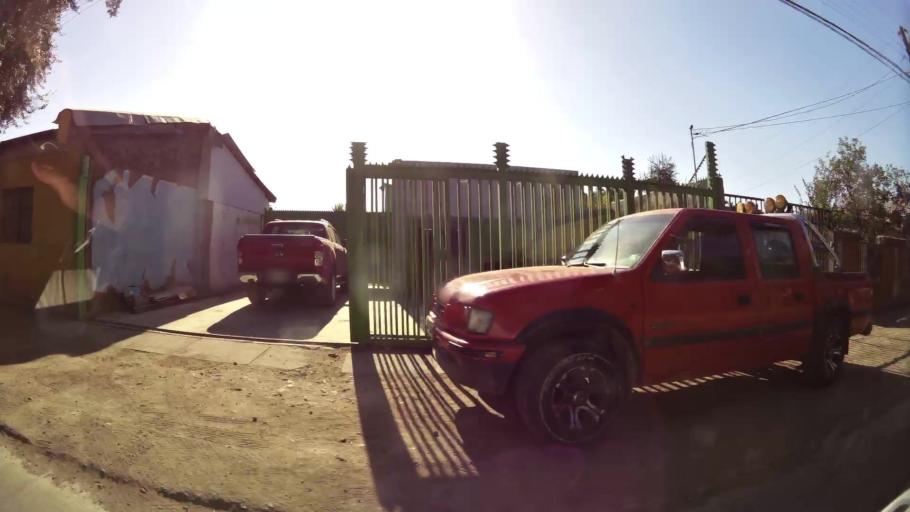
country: CL
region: Maule
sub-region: Provincia de Talca
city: Talca
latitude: -35.4434
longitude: -71.6636
